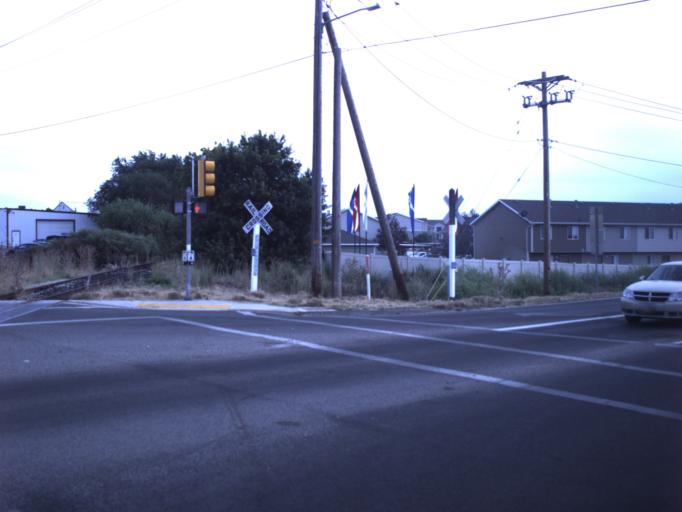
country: US
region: Utah
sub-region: Weber County
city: West Haven
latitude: 41.2054
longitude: -112.0259
